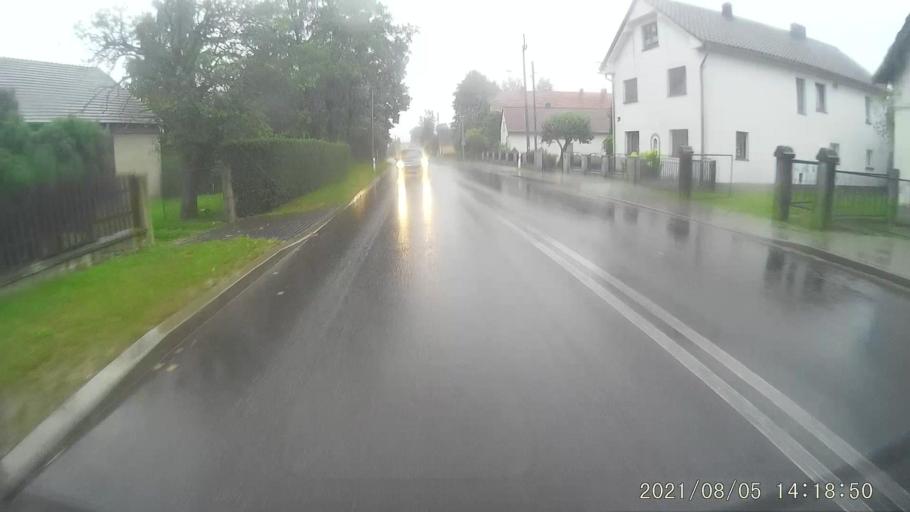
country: PL
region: Opole Voivodeship
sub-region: Powiat prudnicki
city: Biala
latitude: 50.4648
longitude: 17.6910
